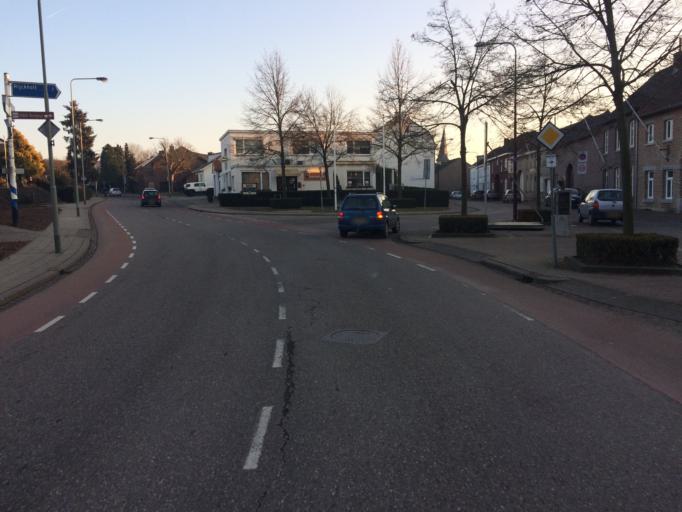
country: NL
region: Limburg
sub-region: Gemeente Maastricht
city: Heer
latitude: 50.8155
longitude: 5.7285
